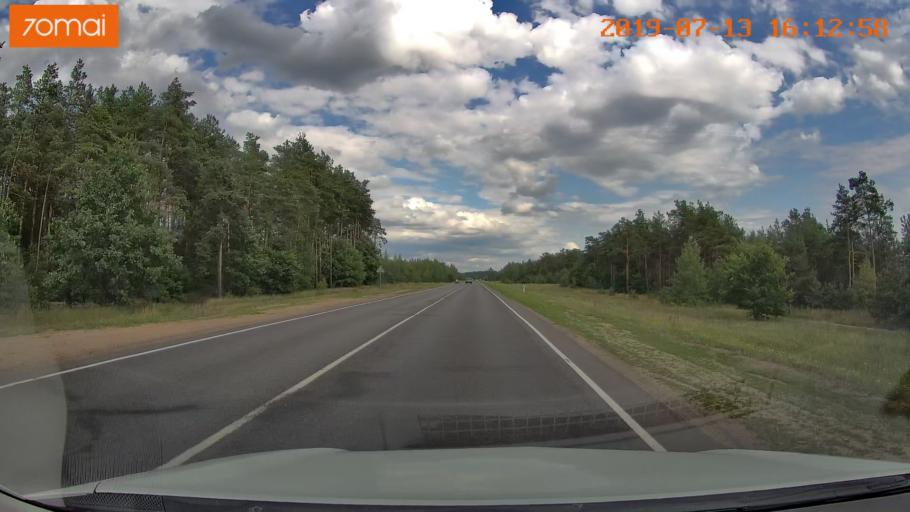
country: BY
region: Mogilev
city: Babruysk
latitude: 53.1649
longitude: 29.2923
